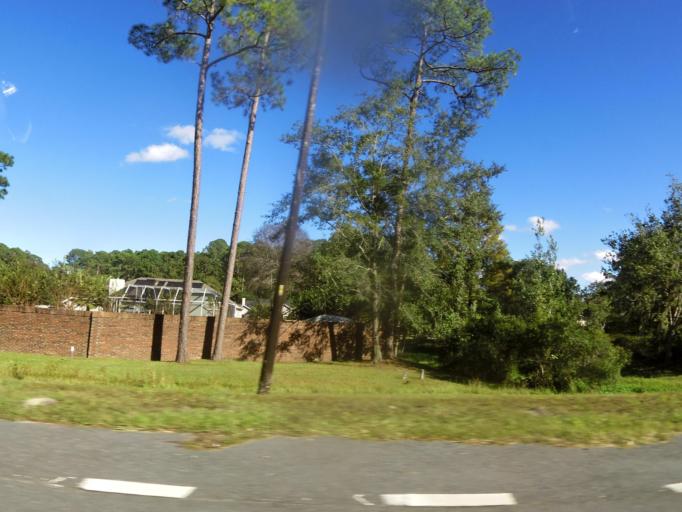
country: US
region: Florida
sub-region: Alachua County
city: Alachua
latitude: 29.7155
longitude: -82.3855
